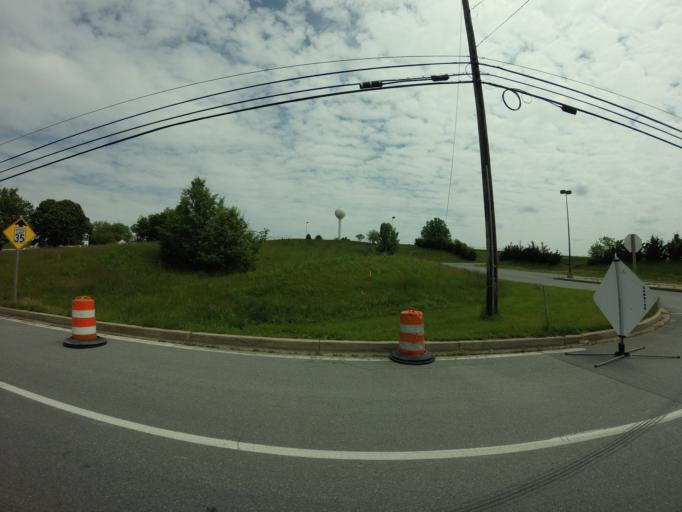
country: US
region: Maryland
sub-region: Frederick County
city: Urbana
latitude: 39.3226
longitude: -77.3399
